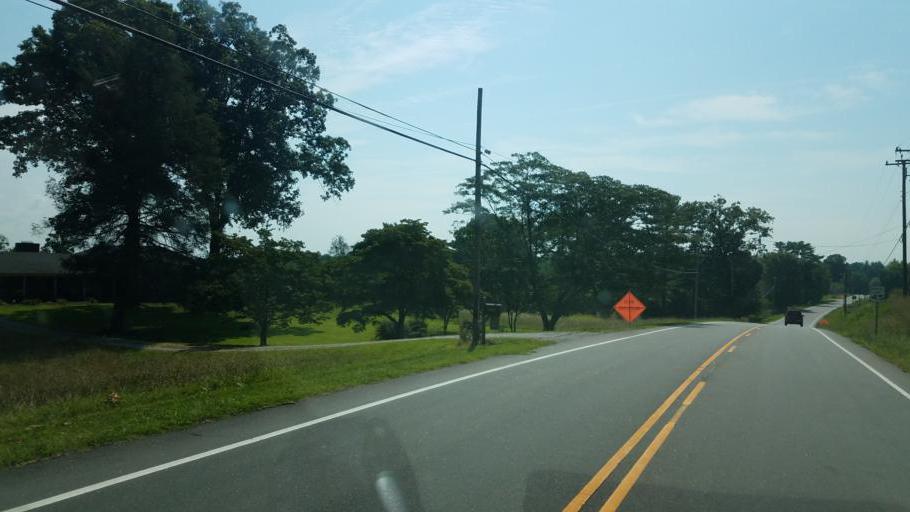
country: US
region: North Carolina
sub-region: Burke County
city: Glen Alpine
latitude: 35.7710
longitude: -81.7486
